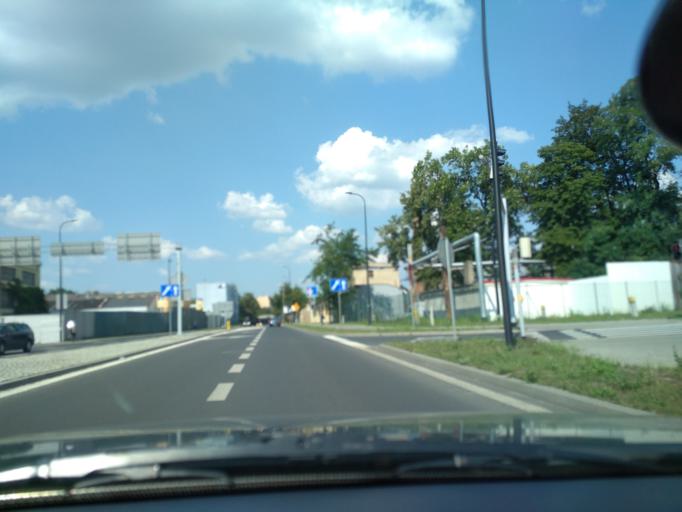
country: PL
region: Silesian Voivodeship
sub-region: Gliwice
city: Gliwice
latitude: 50.3046
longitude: 18.6602
